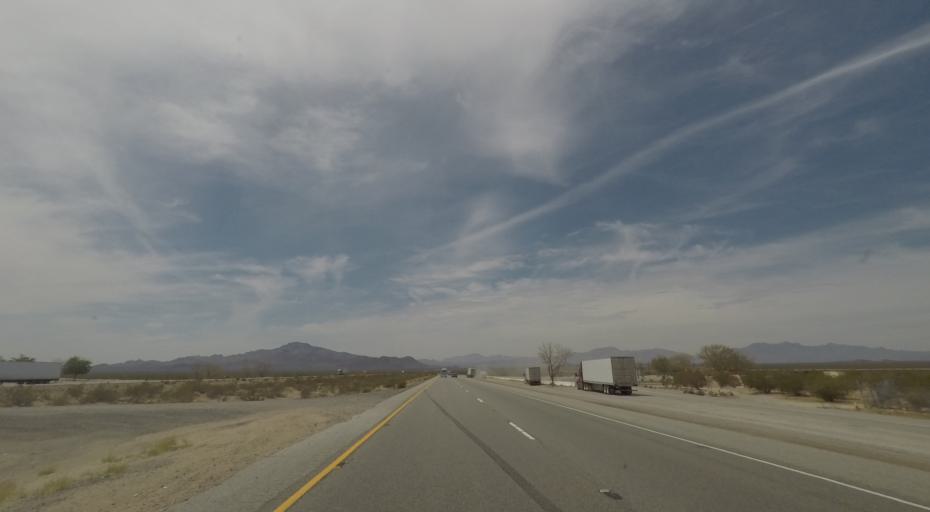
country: US
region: California
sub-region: San Bernardino County
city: Needles
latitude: 34.8097
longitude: -115.2174
